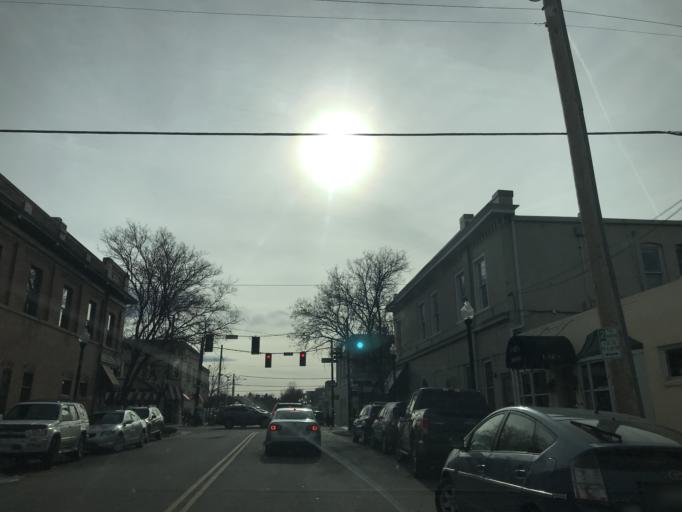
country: US
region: Colorado
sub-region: Arapahoe County
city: Littleton
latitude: 39.6142
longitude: -105.0173
